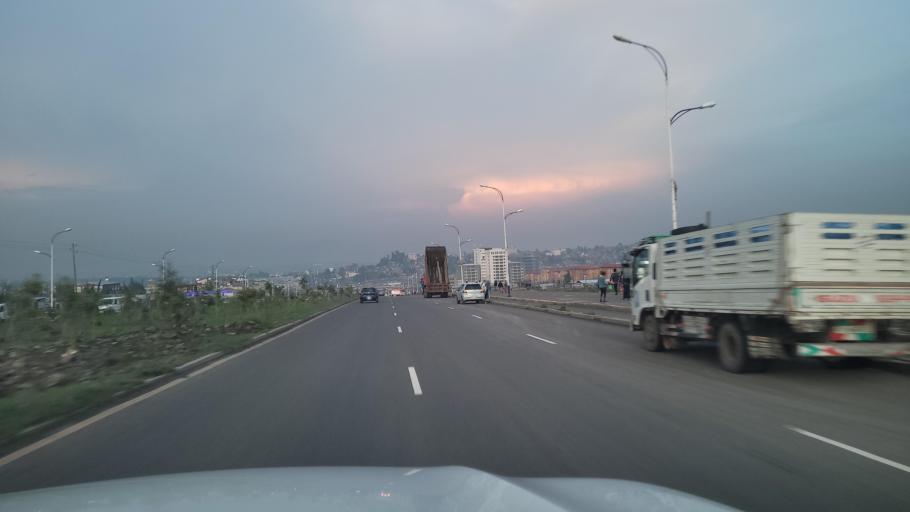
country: ET
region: Adis Abeba
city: Addis Ababa
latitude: 8.9388
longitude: 38.7272
